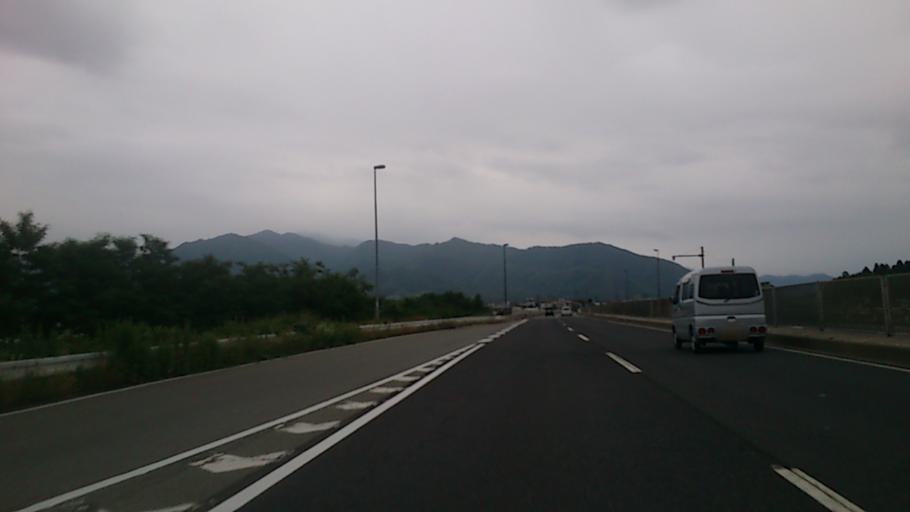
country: JP
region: Yamagata
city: Tendo
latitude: 38.3951
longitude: 140.3776
